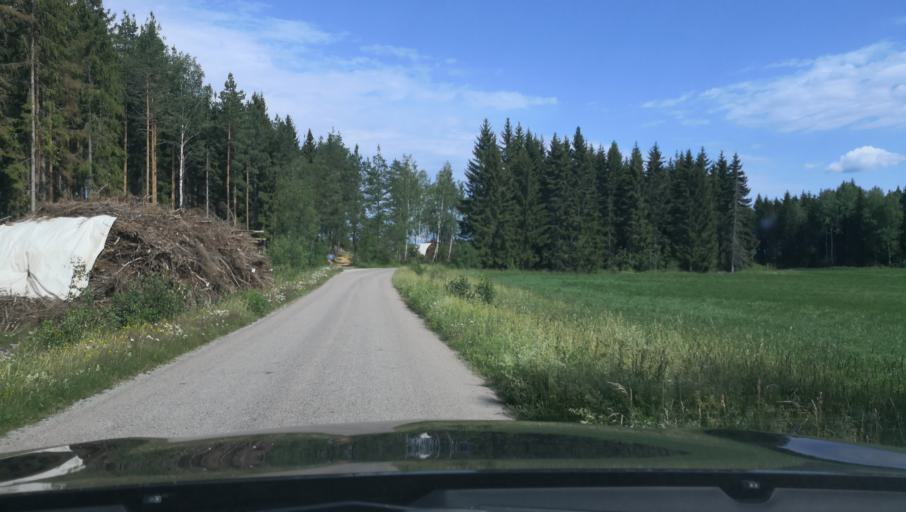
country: SE
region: Vaestmanland
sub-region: Surahammars Kommun
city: Ramnas
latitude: 59.9483
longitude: 16.2083
